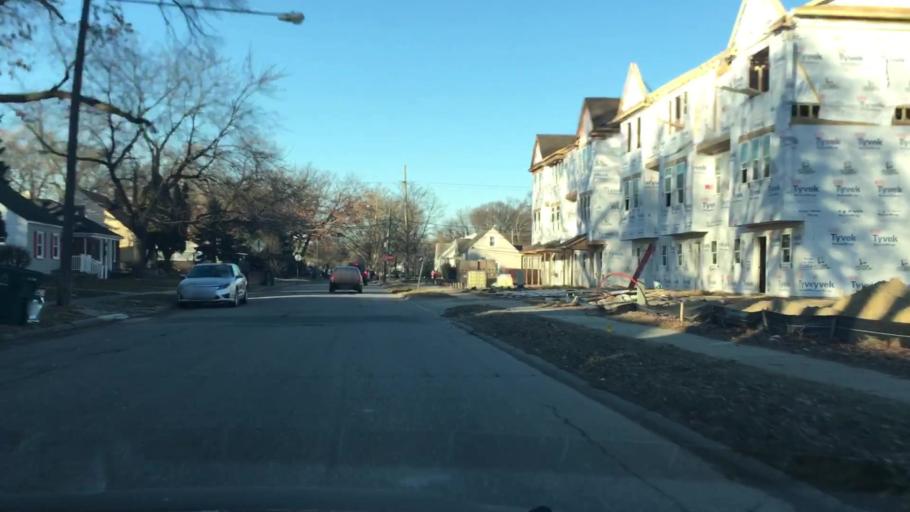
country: US
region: Michigan
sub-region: Oakland County
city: Ferndale
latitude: 42.4486
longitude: -83.1395
